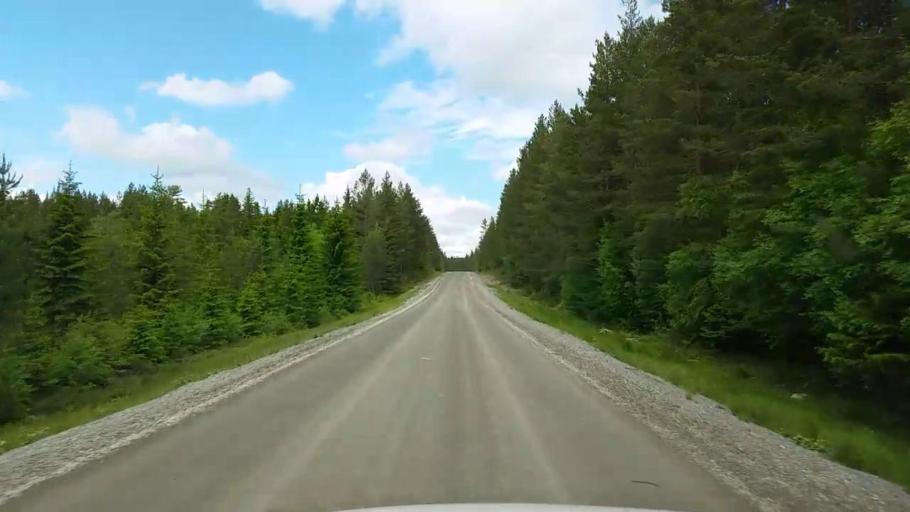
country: SE
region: Gaevleborg
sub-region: Bollnas Kommun
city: Kilafors
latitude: 61.0069
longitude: 16.3857
